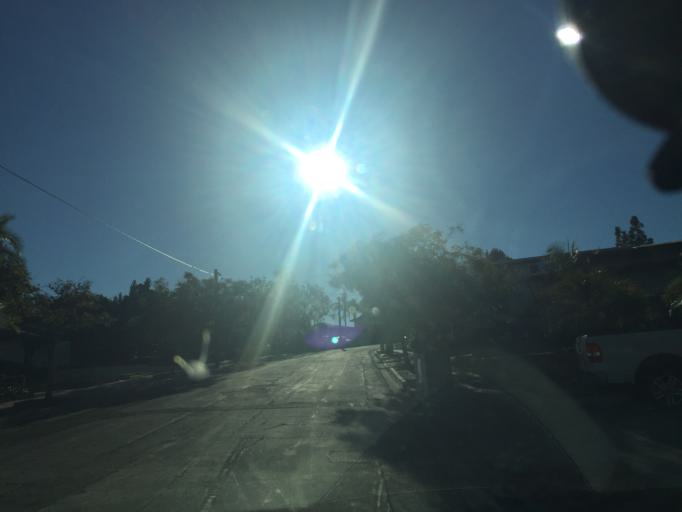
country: US
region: California
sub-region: San Diego County
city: La Mesa
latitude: 32.7789
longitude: -117.0852
